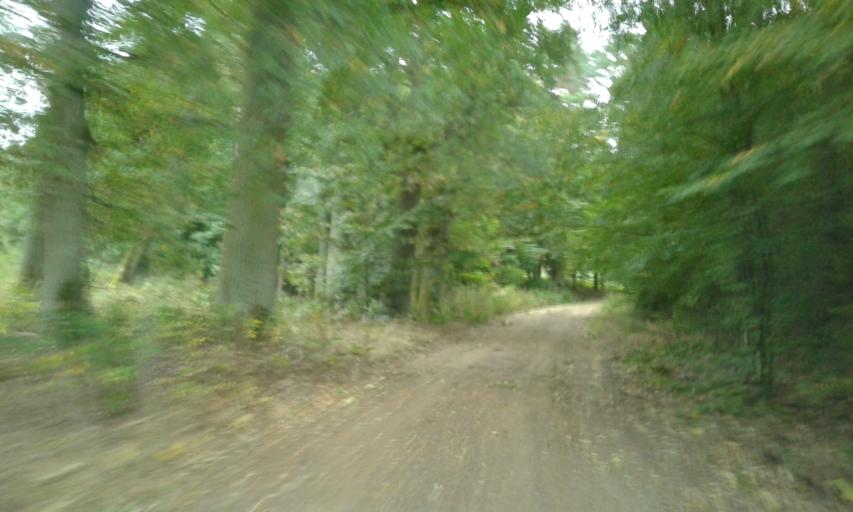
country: PL
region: West Pomeranian Voivodeship
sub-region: Powiat choszczenski
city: Pelczyce
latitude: 53.0846
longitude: 15.2538
